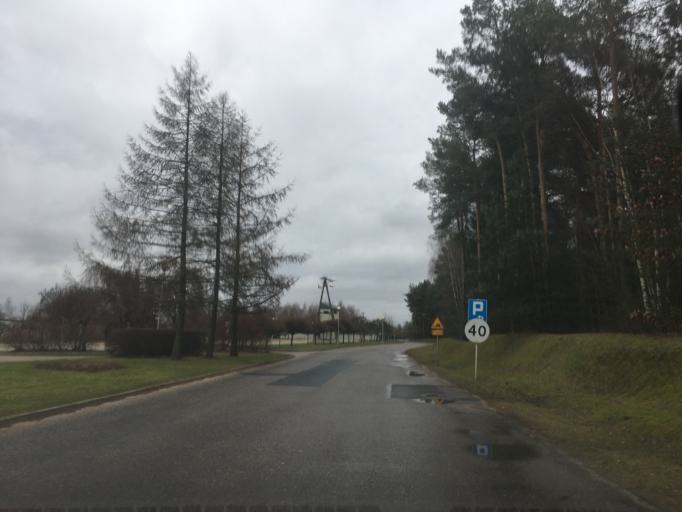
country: PL
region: Masovian Voivodeship
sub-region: Powiat piaseczynski
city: Lesznowola
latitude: 52.0565
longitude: 20.8965
